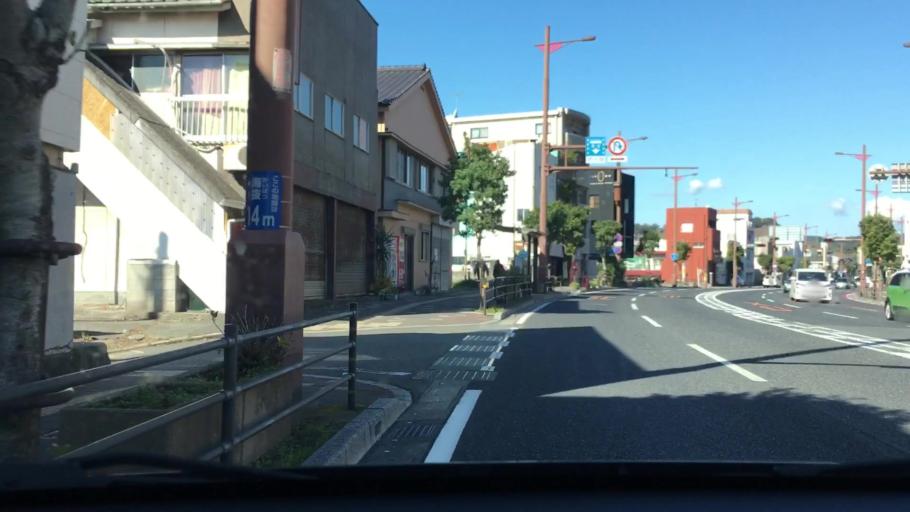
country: JP
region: Kagoshima
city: Kagoshima-shi
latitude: 31.6182
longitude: 130.5272
